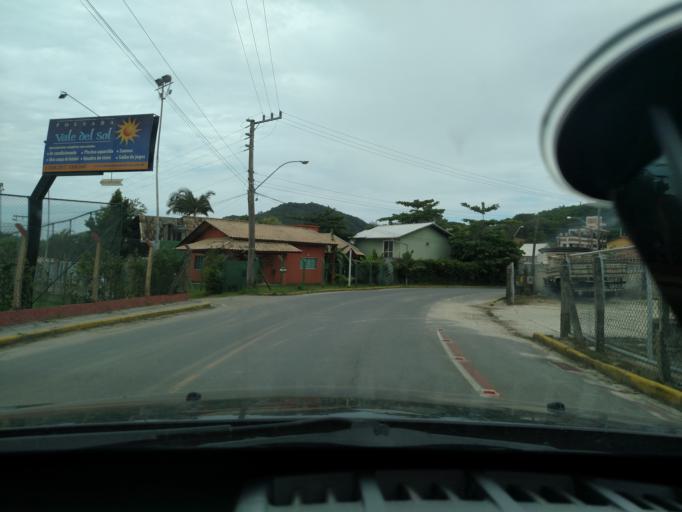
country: BR
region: Santa Catarina
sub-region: Porto Belo
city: Porto Belo
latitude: -27.1555
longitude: -48.4896
